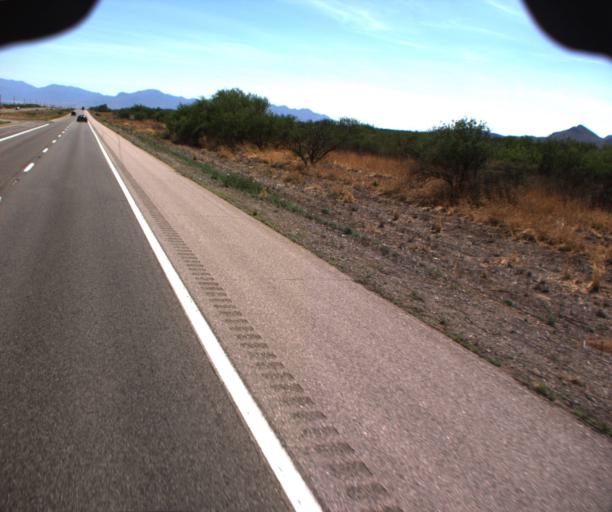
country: US
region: Arizona
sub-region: Cochise County
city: Huachuca City
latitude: 31.7467
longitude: -110.3503
